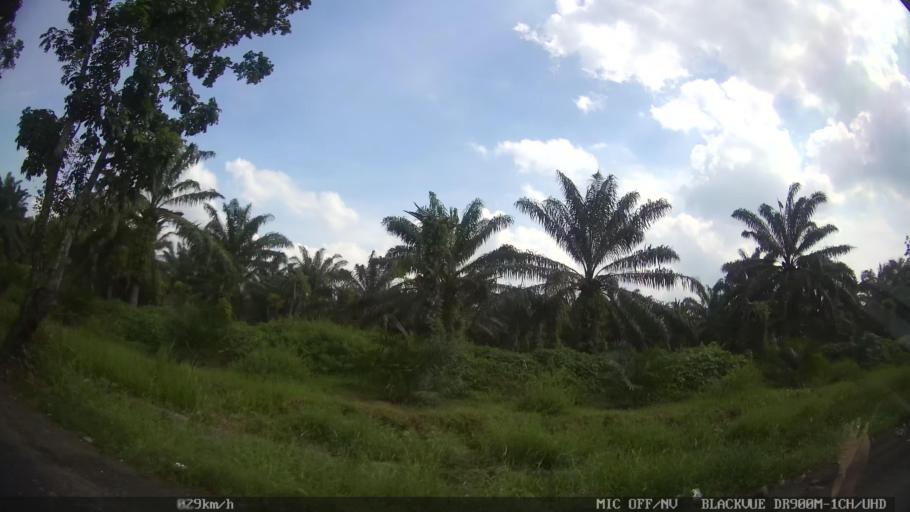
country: ID
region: North Sumatra
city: Binjai
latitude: 3.6503
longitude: 98.5140
